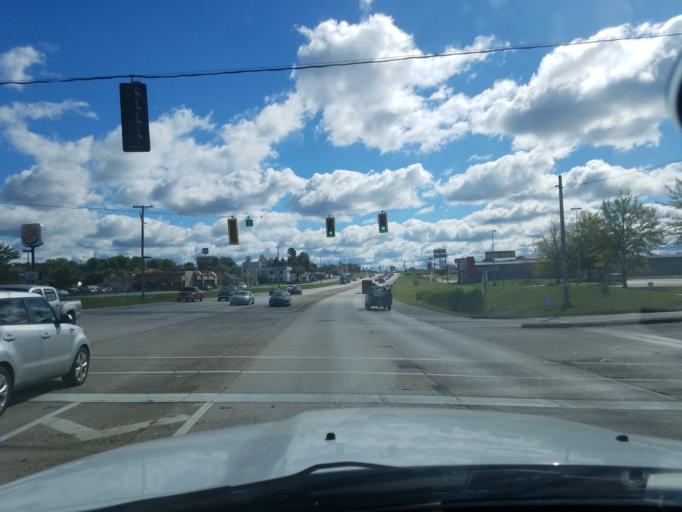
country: US
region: Kentucky
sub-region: Laurel County
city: London
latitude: 37.1106
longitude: -84.0920
